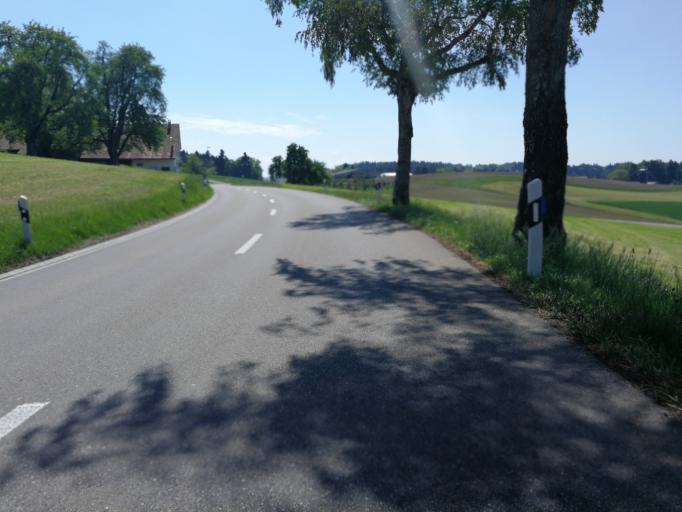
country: CH
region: Zurich
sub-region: Bezirk Uster
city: Aesch
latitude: 47.3158
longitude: 8.6431
